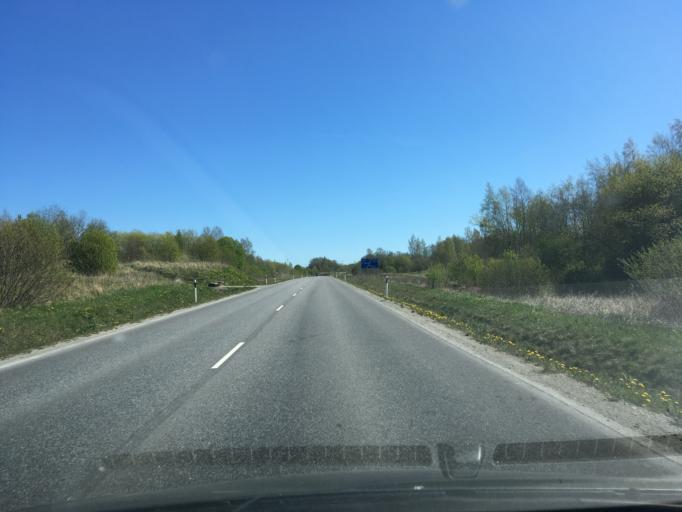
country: EE
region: Harju
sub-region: Maardu linn
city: Maardu
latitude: 59.4540
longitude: 25.0229
